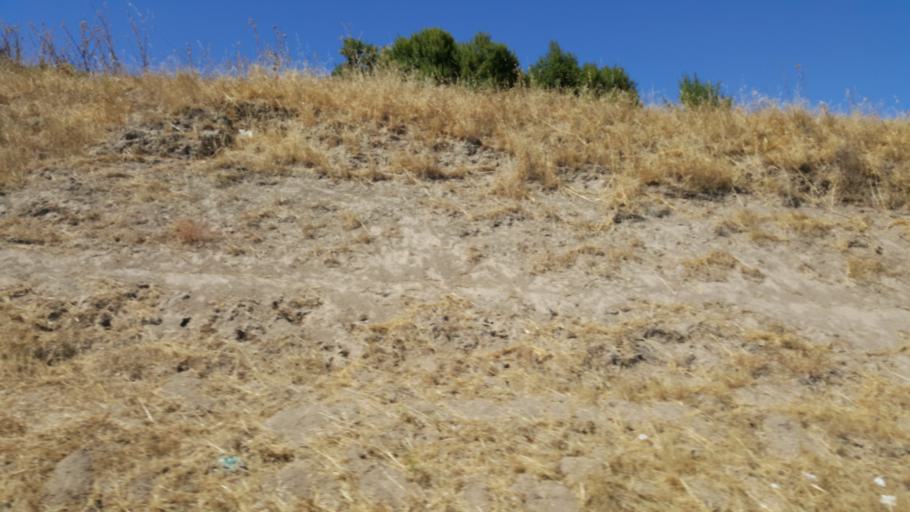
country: US
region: California
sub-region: San Mateo County
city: Woodside
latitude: 37.4185
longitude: -122.2285
